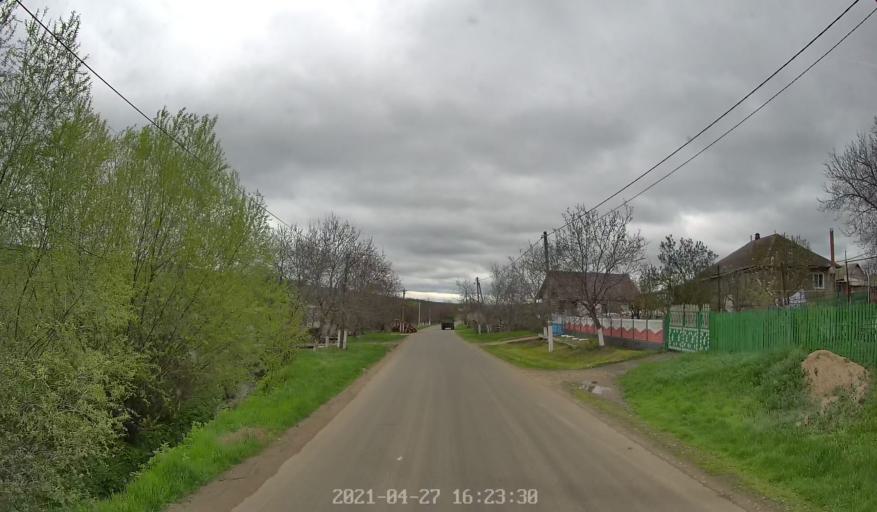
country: MD
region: Chisinau
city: Singera
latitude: 46.9984
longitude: 29.0179
